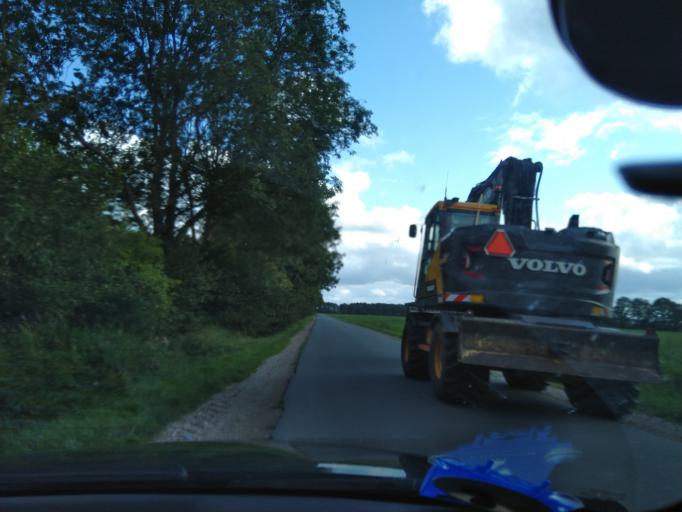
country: NL
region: Drenthe
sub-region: Gemeente Tynaarlo
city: Vries
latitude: 53.0869
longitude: 6.5365
